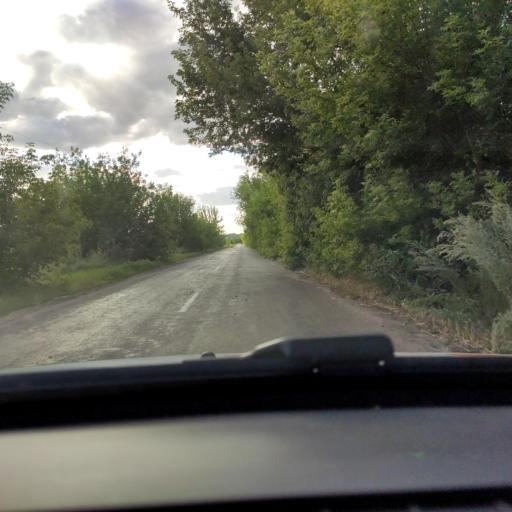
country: RU
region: Voronezj
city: Orlovo
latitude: 51.6422
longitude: 39.7441
